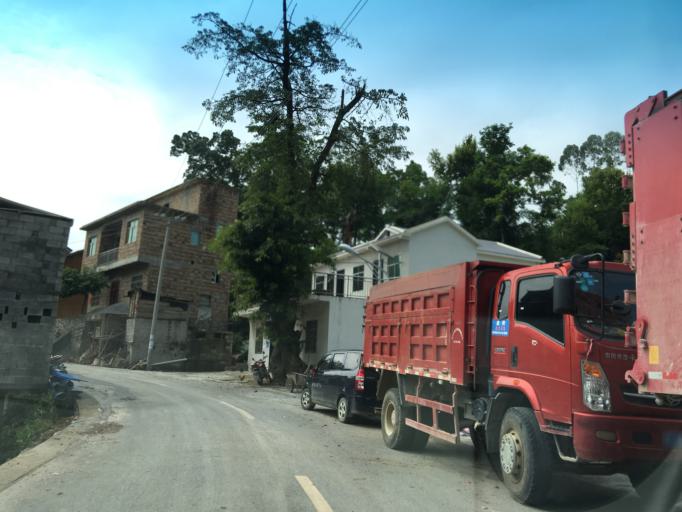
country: CN
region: Guangxi Zhuangzu Zizhiqu
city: Xinzhou
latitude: 24.8230
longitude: 105.6430
